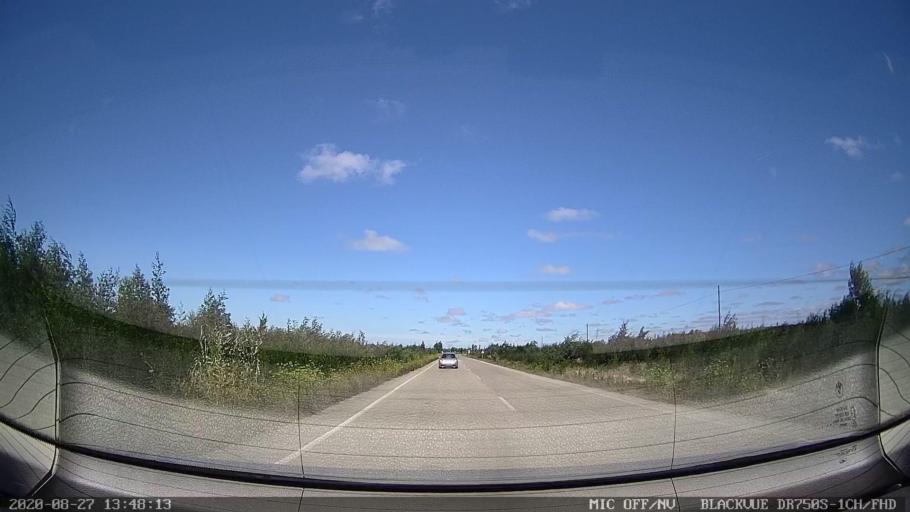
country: PT
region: Coimbra
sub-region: Mira
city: Mira
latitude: 40.3803
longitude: -8.7445
